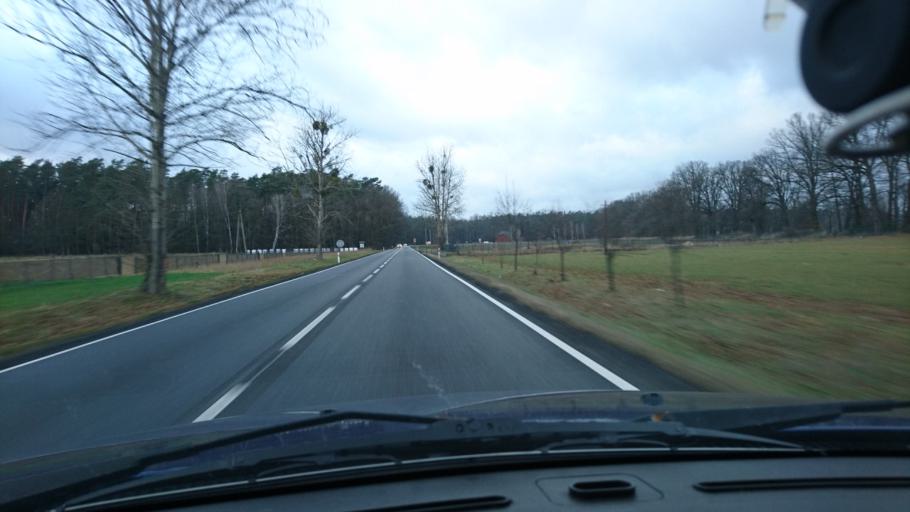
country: PL
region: Opole Voivodeship
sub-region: Powiat oleski
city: Olesno
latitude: 50.9182
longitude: 18.3438
